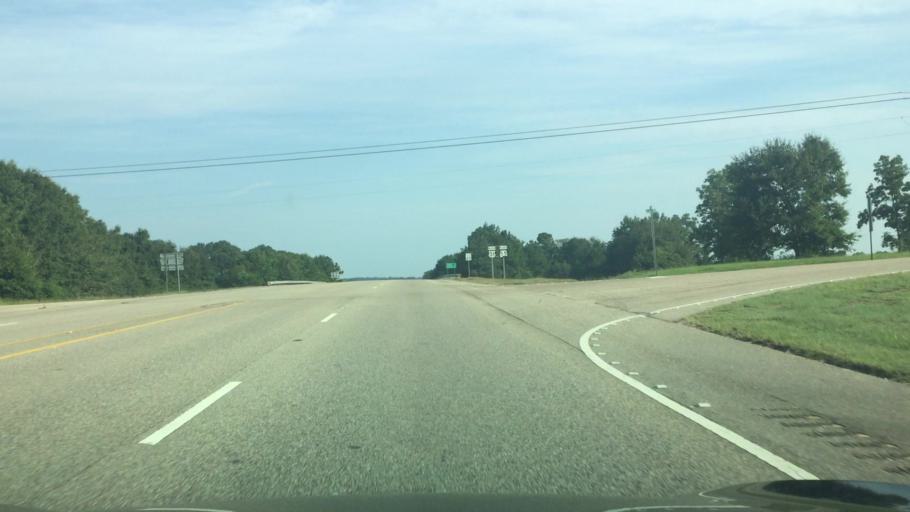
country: US
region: Alabama
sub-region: Butler County
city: Georgiana
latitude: 31.5401
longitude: -86.7281
